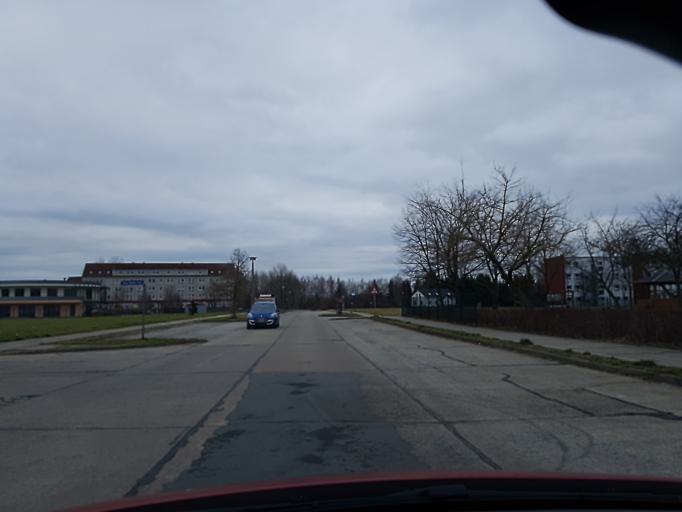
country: DE
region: Brandenburg
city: Elsterwerda
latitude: 51.4620
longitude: 13.5038
